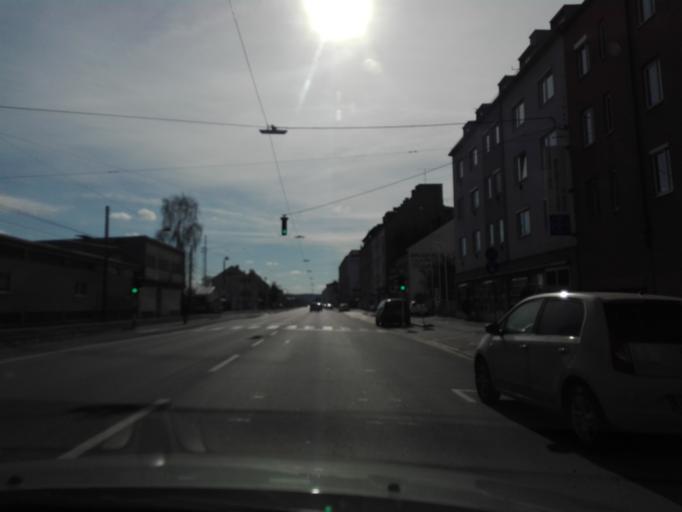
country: AT
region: Upper Austria
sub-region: Linz Stadt
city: Linz
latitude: 48.2693
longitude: 14.3158
